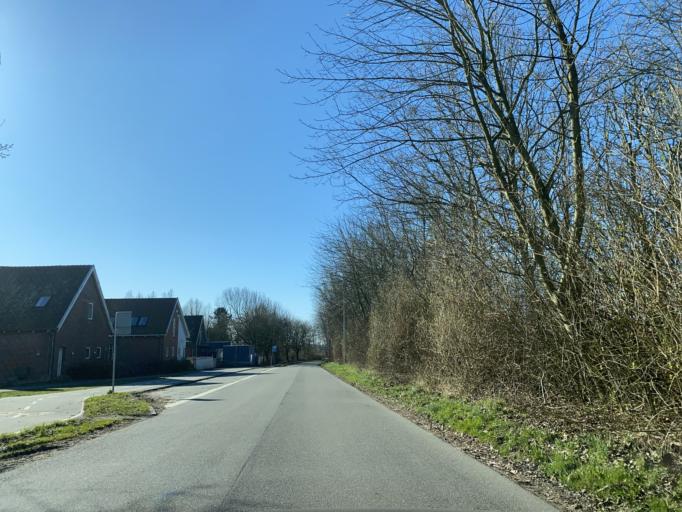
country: DK
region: Central Jutland
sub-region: Skanderborg Kommune
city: Skovby
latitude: 56.1900
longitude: 9.9637
